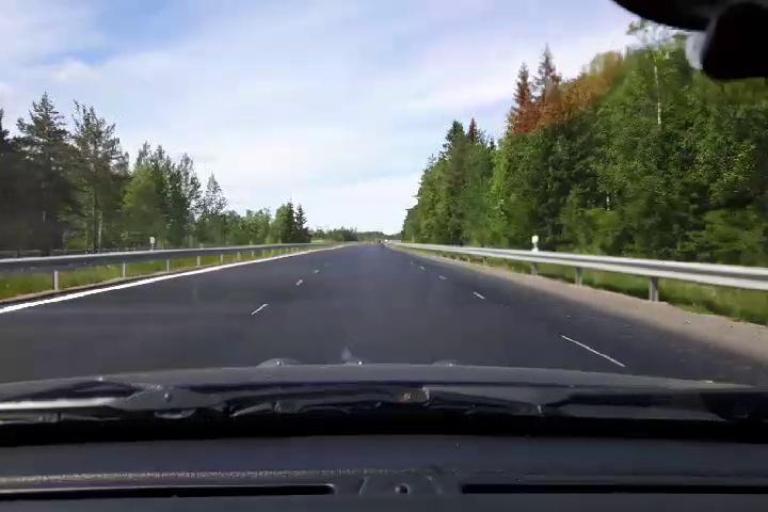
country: SE
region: Gaevleborg
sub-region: Gavle Kommun
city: Gavle
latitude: 60.6220
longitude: 17.1588
